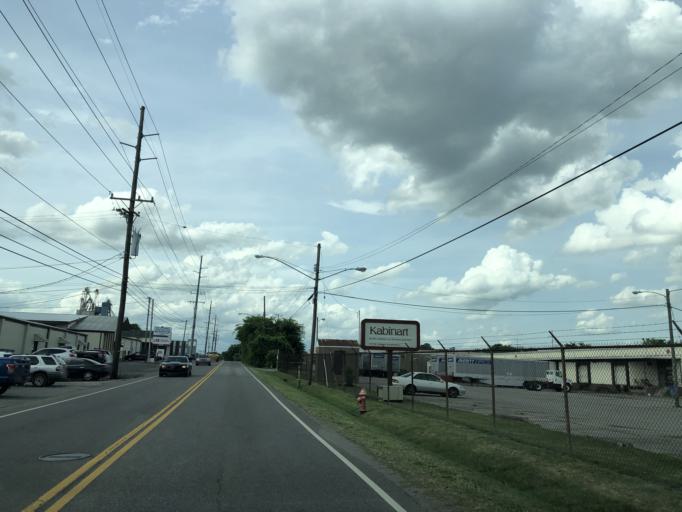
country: US
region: Tennessee
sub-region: Davidson County
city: Oak Hill
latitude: 36.0925
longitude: -86.7499
